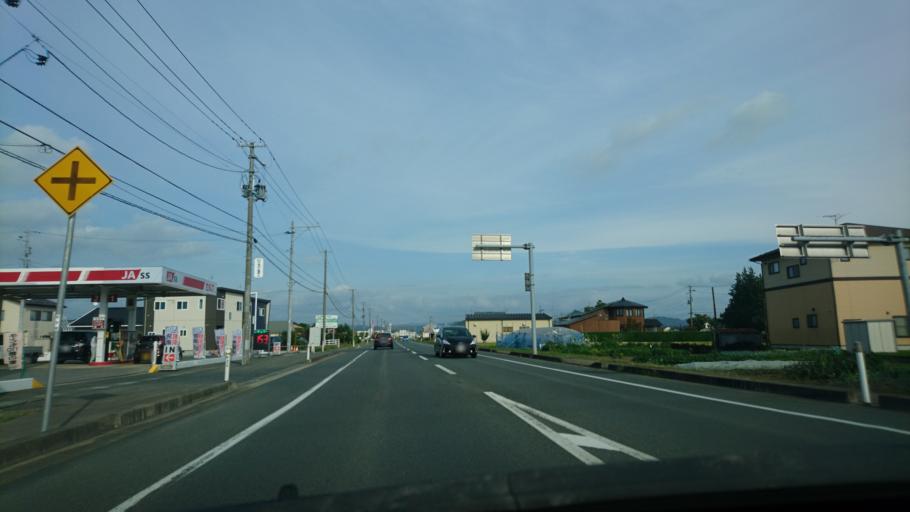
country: JP
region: Iwate
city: Kitakami
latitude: 39.3010
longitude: 141.0725
